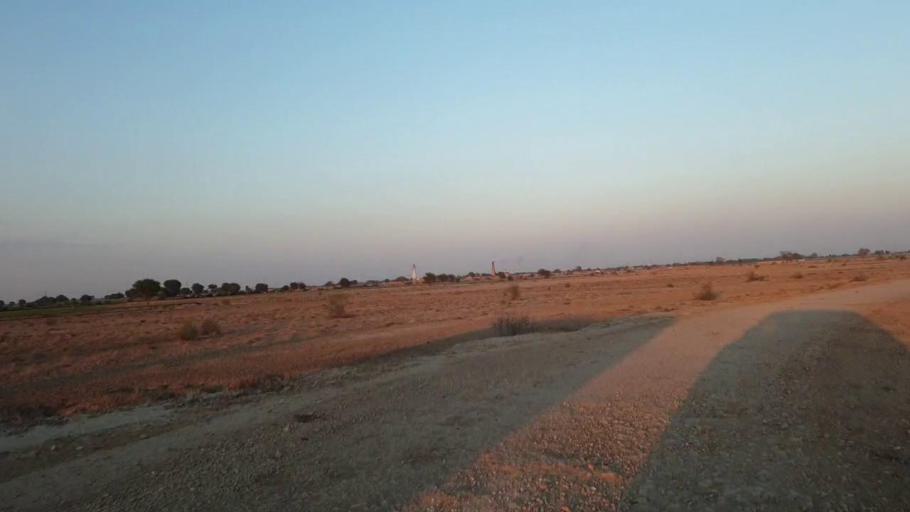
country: PK
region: Sindh
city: Shahpur Chakar
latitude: 26.1683
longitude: 68.5533
